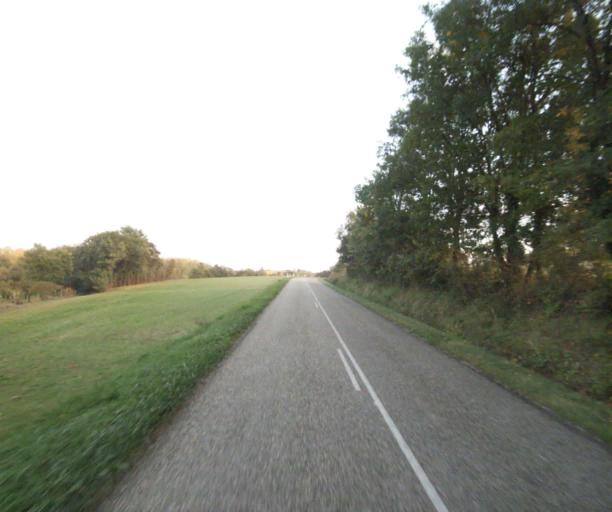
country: FR
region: Midi-Pyrenees
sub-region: Departement du Gers
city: Vic-Fezensac
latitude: 43.7911
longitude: 0.2551
